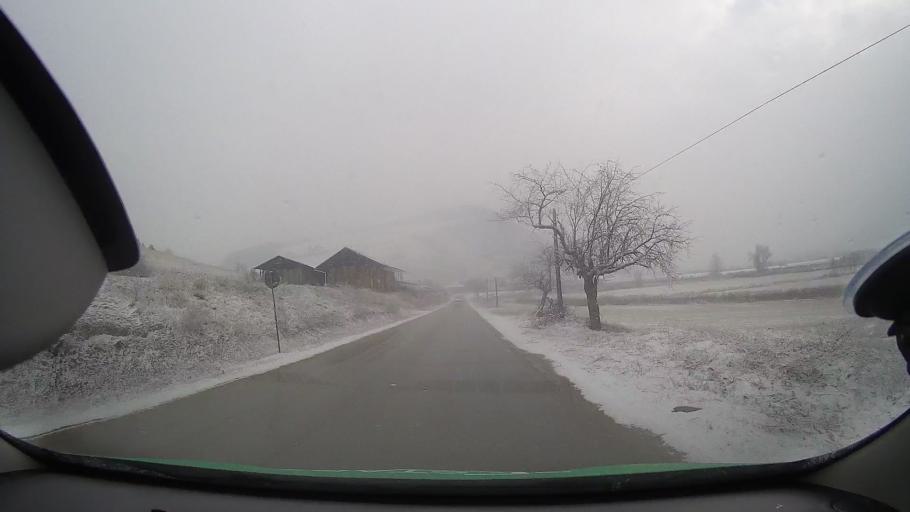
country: RO
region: Alba
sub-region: Comuna Lopadea Noua
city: Lopadea Noua
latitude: 46.2995
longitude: 23.8091
